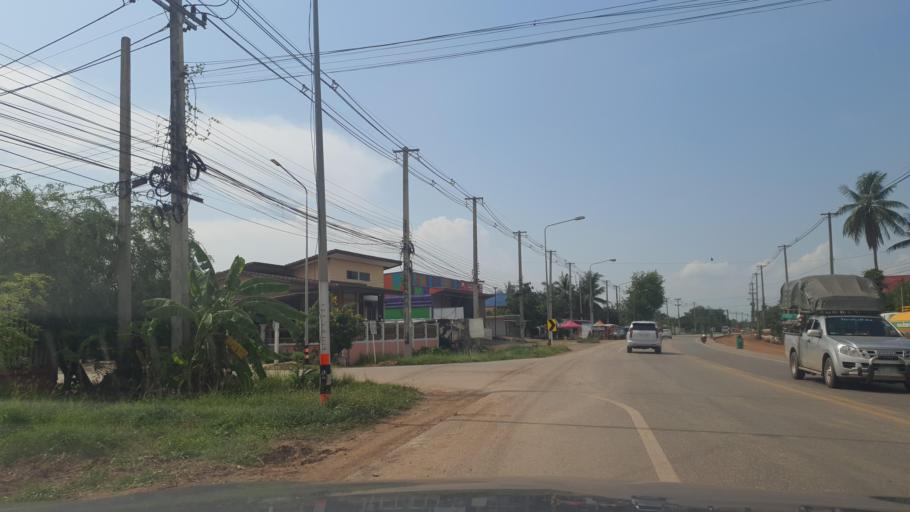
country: TH
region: Sukhothai
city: Si Samrong
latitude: 17.1385
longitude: 99.8499
